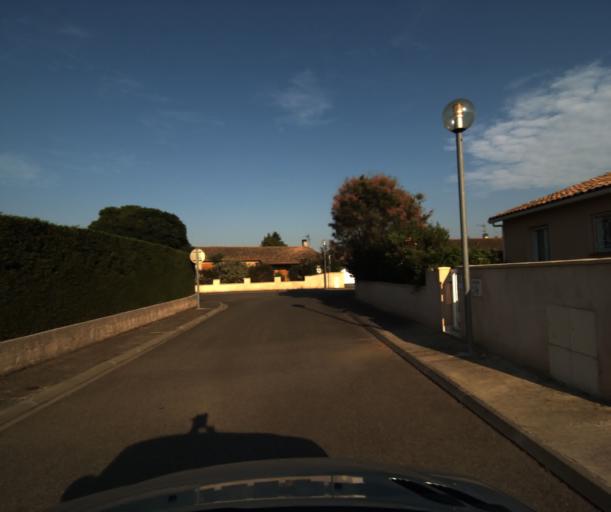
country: FR
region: Midi-Pyrenees
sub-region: Departement de la Haute-Garonne
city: Roquettes
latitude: 43.4825
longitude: 1.3807
